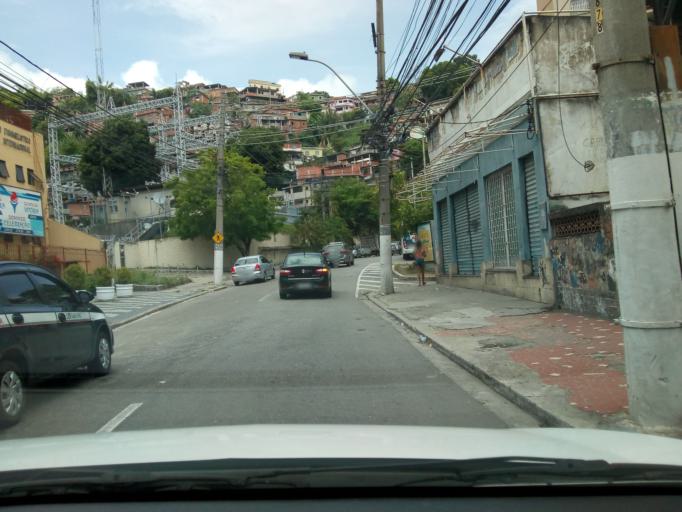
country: BR
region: Rio de Janeiro
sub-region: Niteroi
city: Niteroi
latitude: -22.9100
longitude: -43.1017
